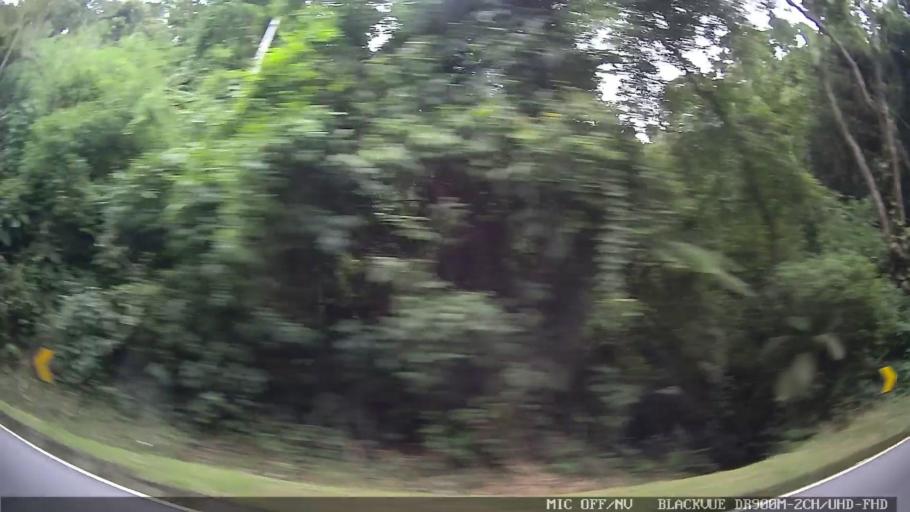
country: BR
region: Sao Paulo
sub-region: Caraguatatuba
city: Caraguatatuba
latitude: -23.5908
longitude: -45.4431
